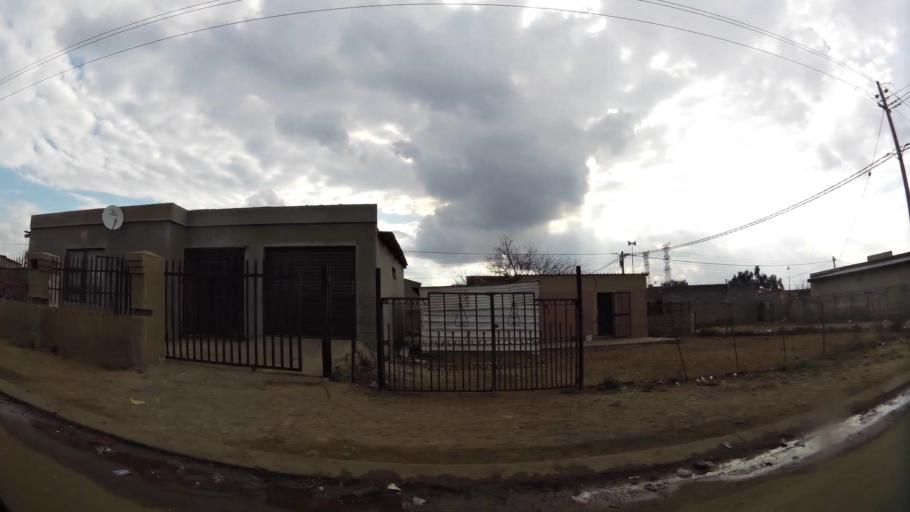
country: ZA
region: Gauteng
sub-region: Sedibeng District Municipality
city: Vanderbijlpark
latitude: -26.6754
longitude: 27.8555
